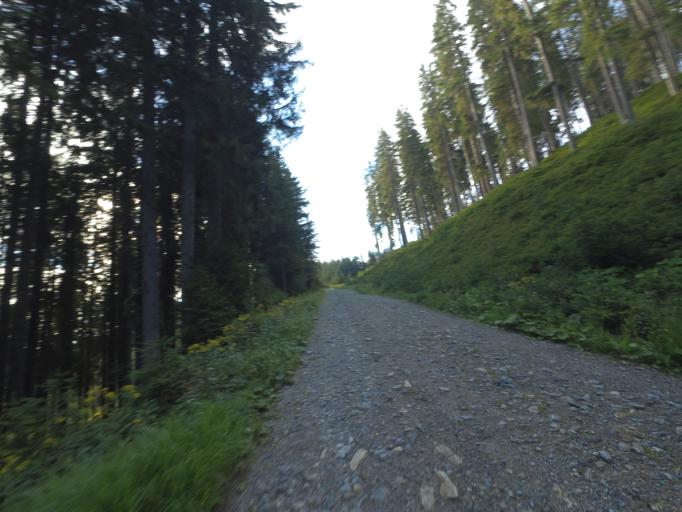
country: AT
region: Salzburg
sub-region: Politischer Bezirk Sankt Johann im Pongau
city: Goldegg
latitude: 47.3506
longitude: 13.0956
